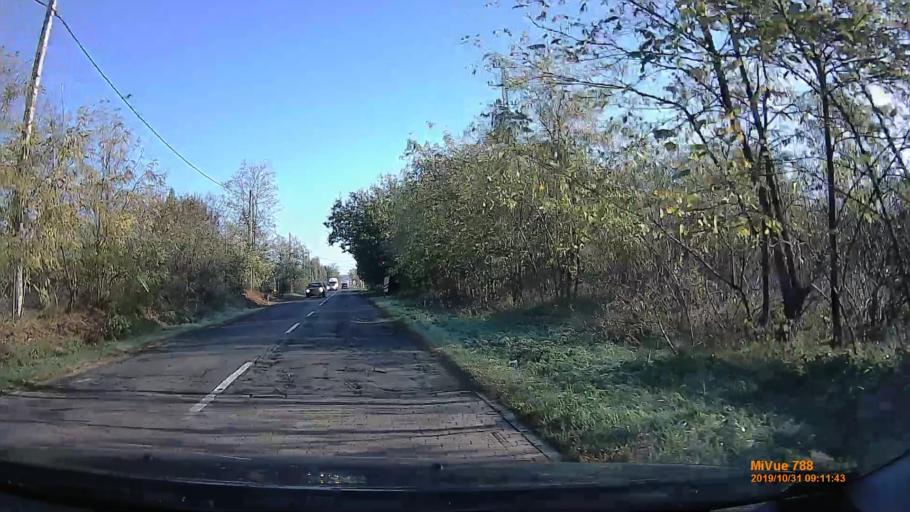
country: HU
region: Pest
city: Peteri
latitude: 47.3689
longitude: 19.3890
